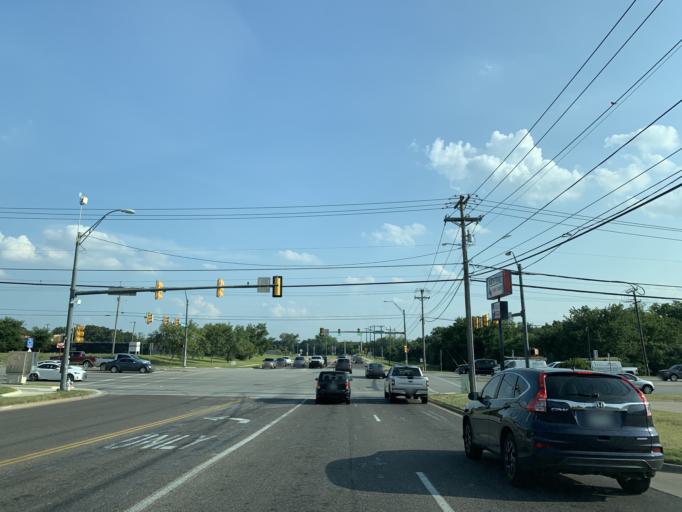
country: US
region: Texas
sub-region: Tarrant County
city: Hurst
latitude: 32.8097
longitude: -97.1867
